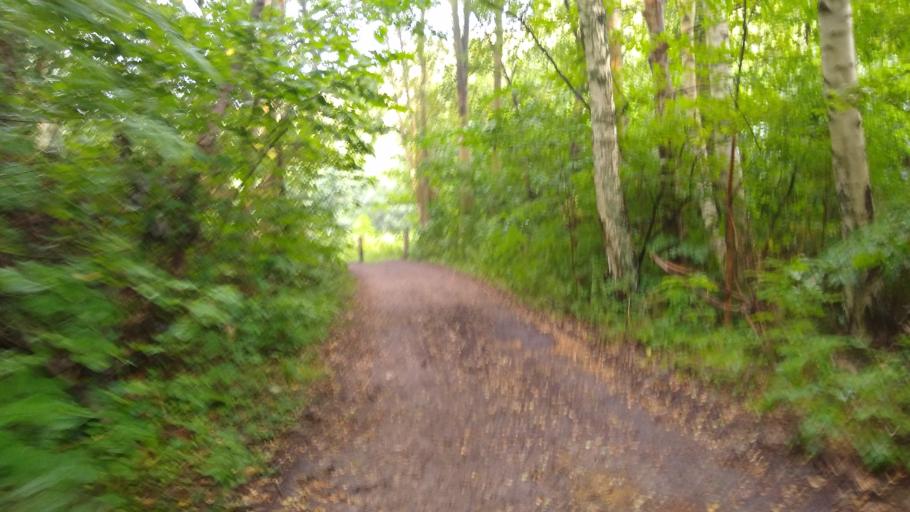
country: DK
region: South Denmark
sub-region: Fredericia Kommune
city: Fredericia
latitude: 55.6061
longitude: 9.7089
